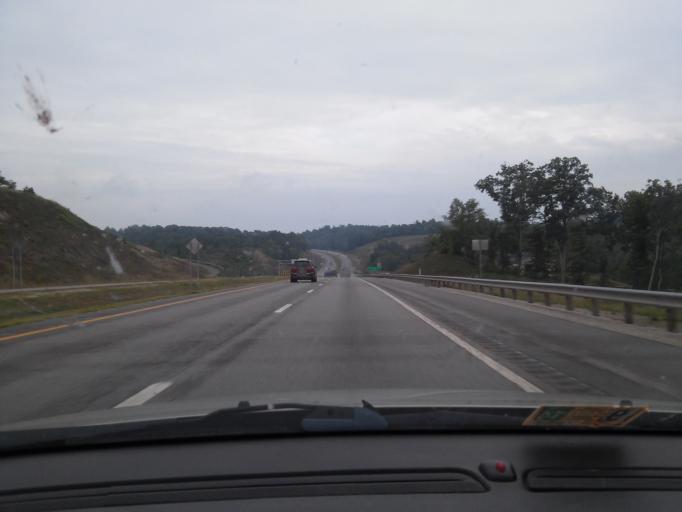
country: US
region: West Virginia
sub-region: Putnam County
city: Buffalo
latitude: 38.5729
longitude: -82.0151
